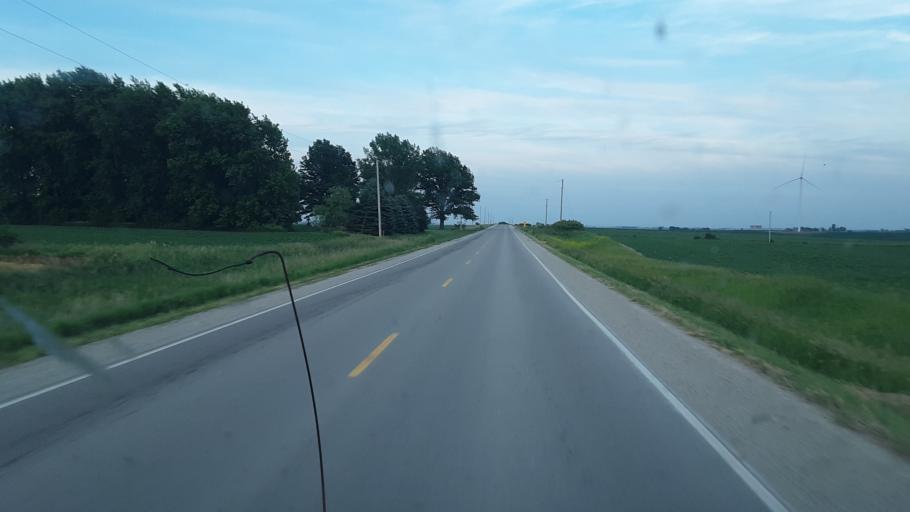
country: US
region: Iowa
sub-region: Iowa County
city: Marengo
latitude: 41.7028
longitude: -92.1704
